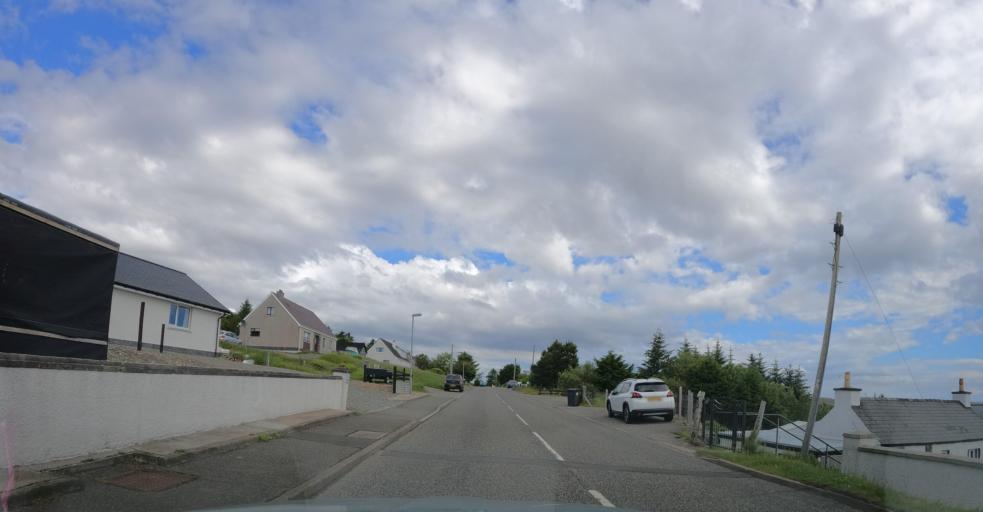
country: GB
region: Scotland
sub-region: Eilean Siar
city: Isle of Lewis
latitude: 58.2433
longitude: -6.3911
